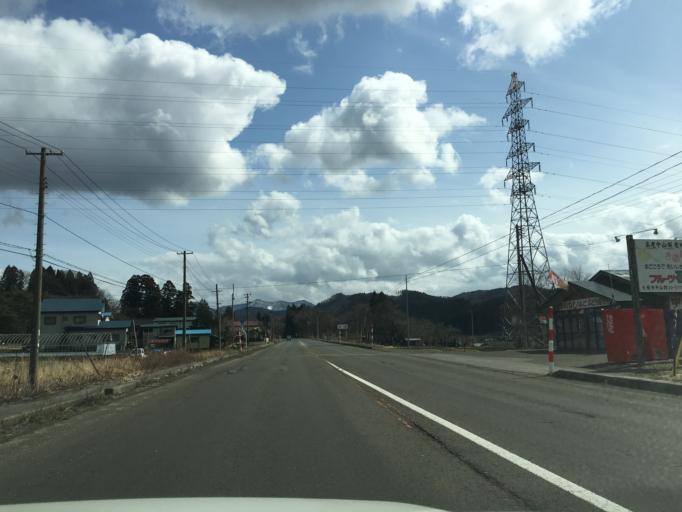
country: JP
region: Akita
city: Odate
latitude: 40.2271
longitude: 140.5996
